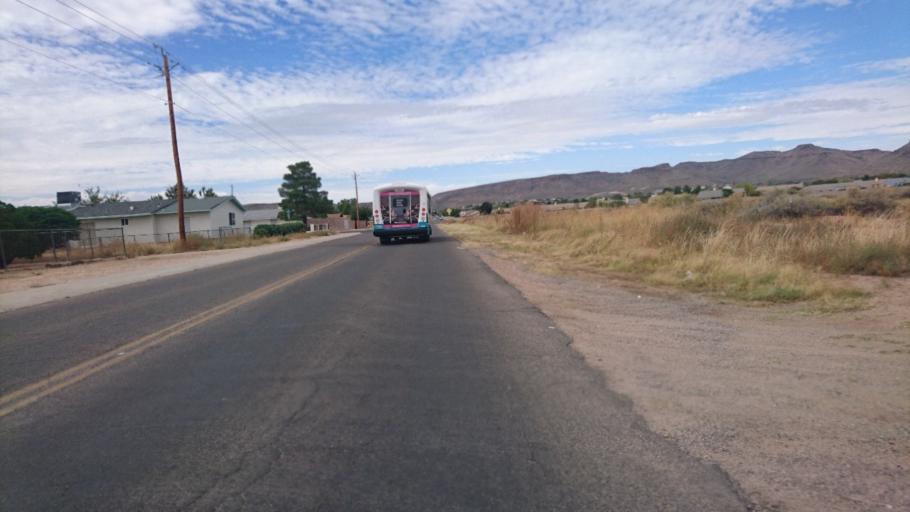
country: US
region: Arizona
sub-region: Mohave County
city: New Kingman-Butler
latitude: 35.2321
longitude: -114.0259
